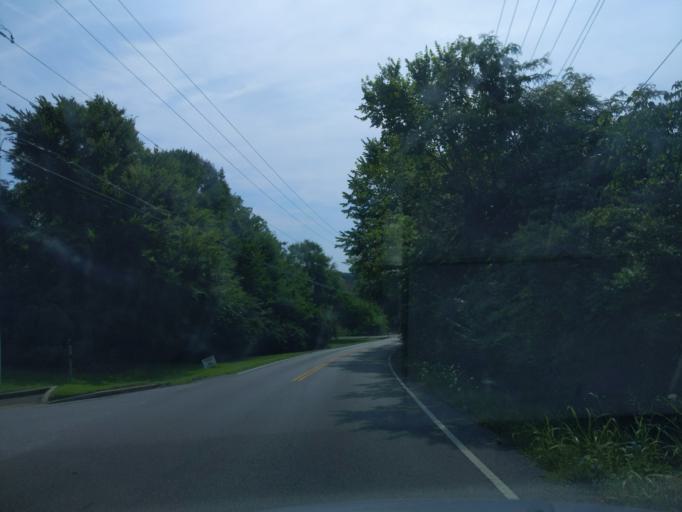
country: US
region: Tennessee
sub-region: Williamson County
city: Brentwood Estates
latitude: 36.0201
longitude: -86.7474
